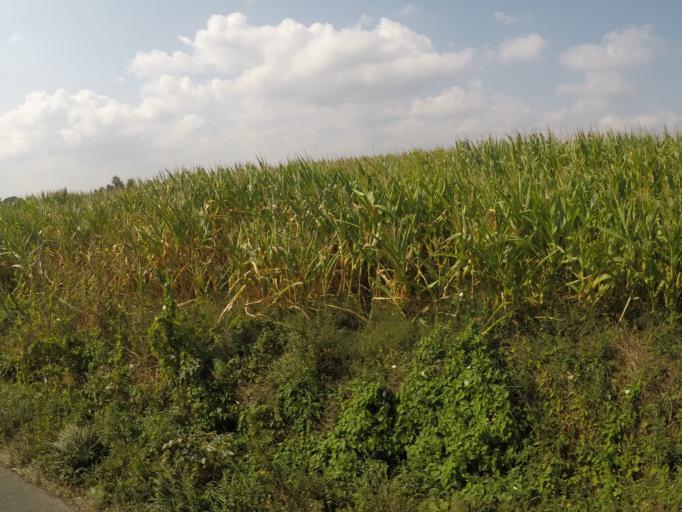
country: FR
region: Brittany
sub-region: Departement des Cotes-d'Armor
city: Tremuson
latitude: 48.5317
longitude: -2.8926
